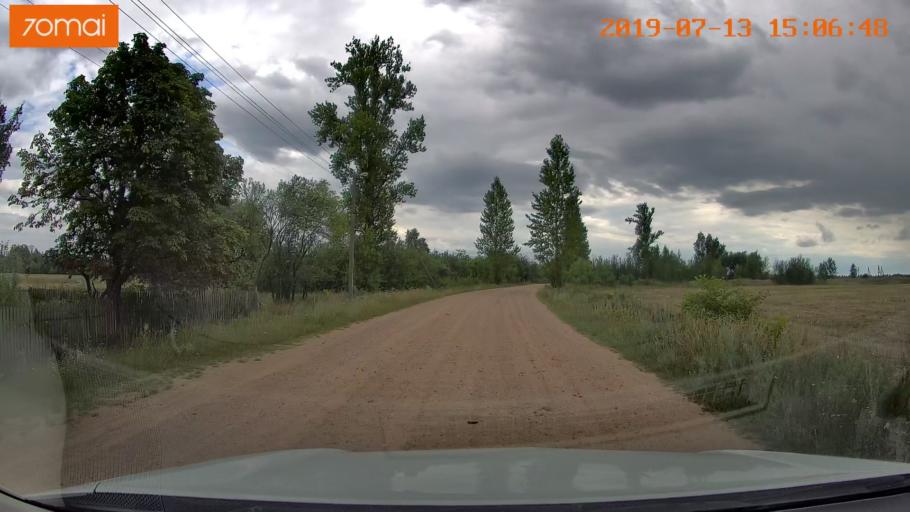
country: BY
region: Mogilev
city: Hlusha
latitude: 53.1959
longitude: 28.7561
